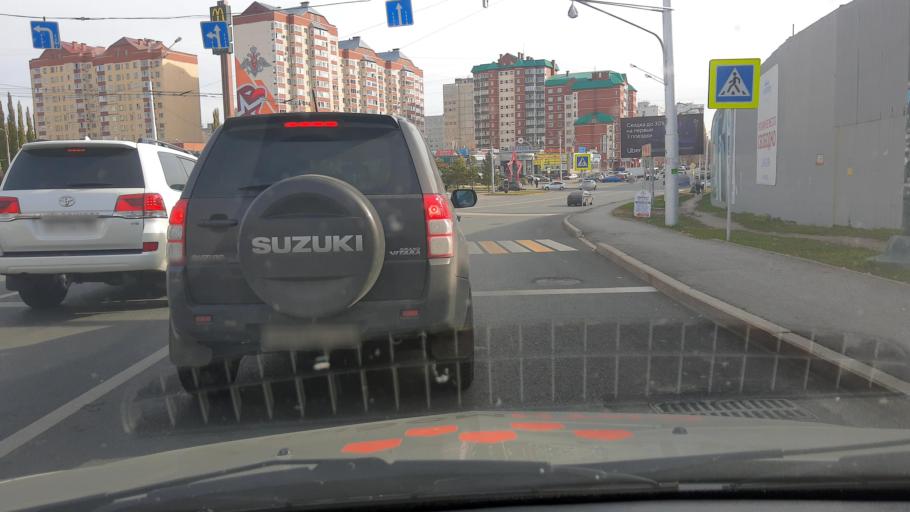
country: RU
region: Bashkortostan
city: Ufa
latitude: 54.6977
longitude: 55.9933
